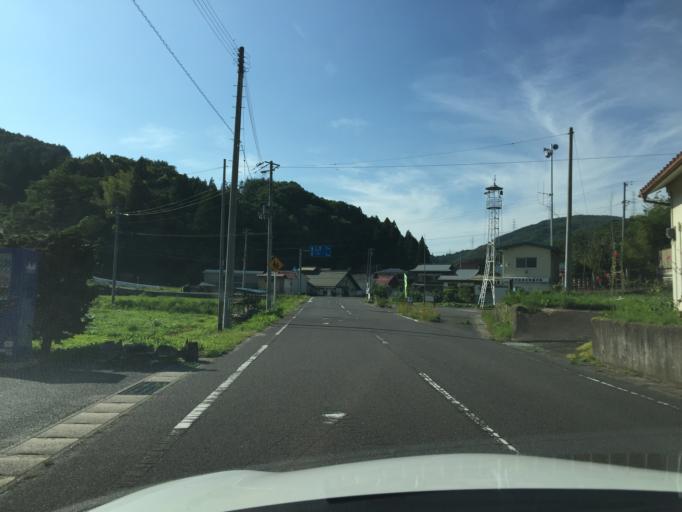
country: JP
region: Fukushima
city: Ishikawa
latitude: 37.2365
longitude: 140.4941
